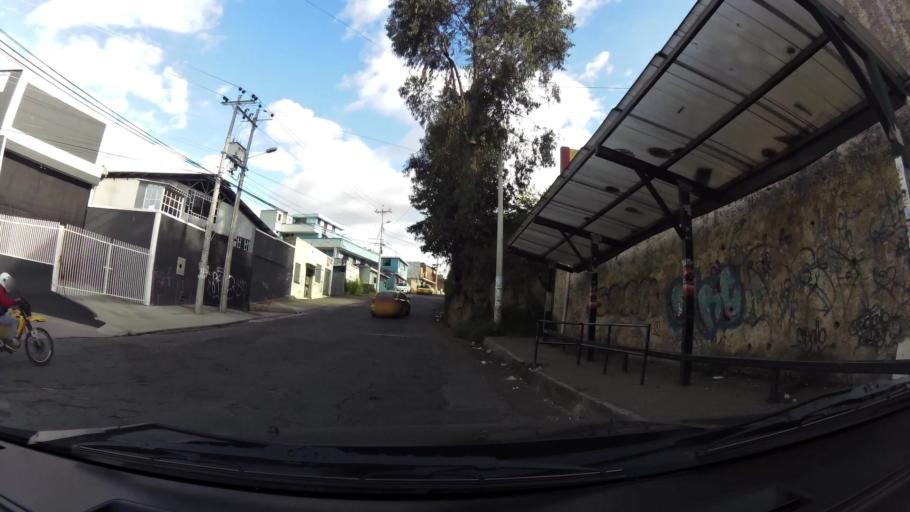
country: EC
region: Pichincha
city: Quito
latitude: -0.1389
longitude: -78.4593
